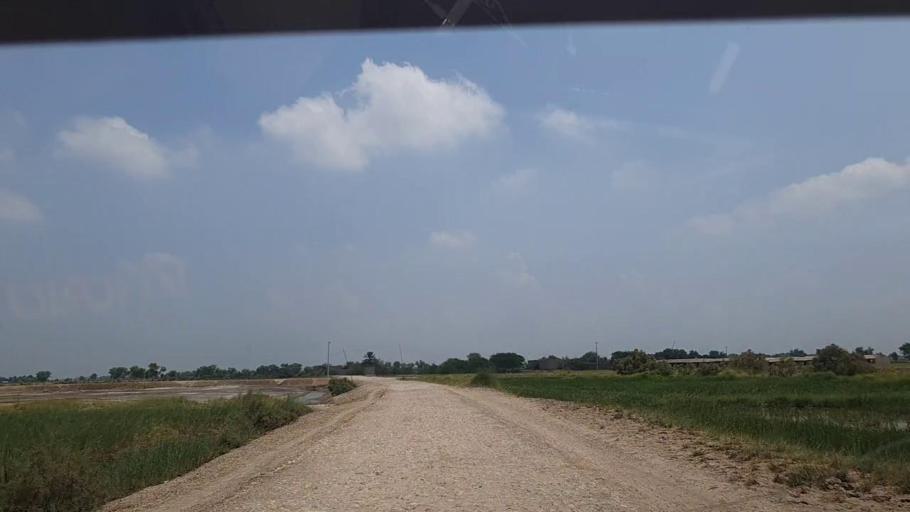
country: PK
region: Sindh
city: Khanpur
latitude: 27.8935
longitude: 69.3988
